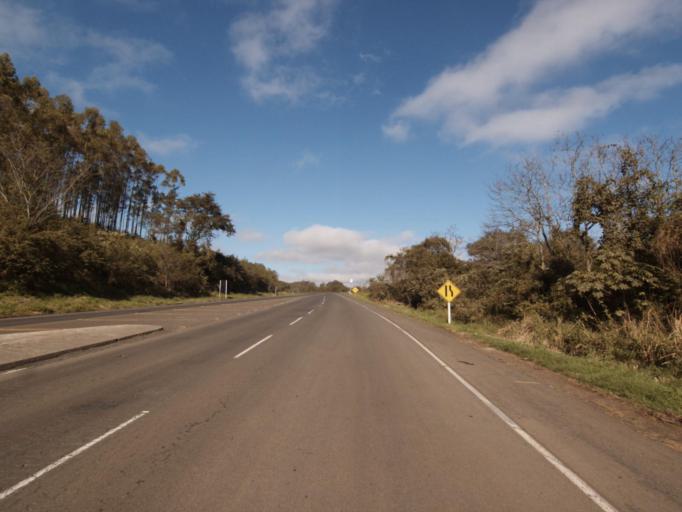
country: BR
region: Rio Grande do Sul
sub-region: Frederico Westphalen
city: Frederico Westphalen
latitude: -27.0711
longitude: -53.2306
